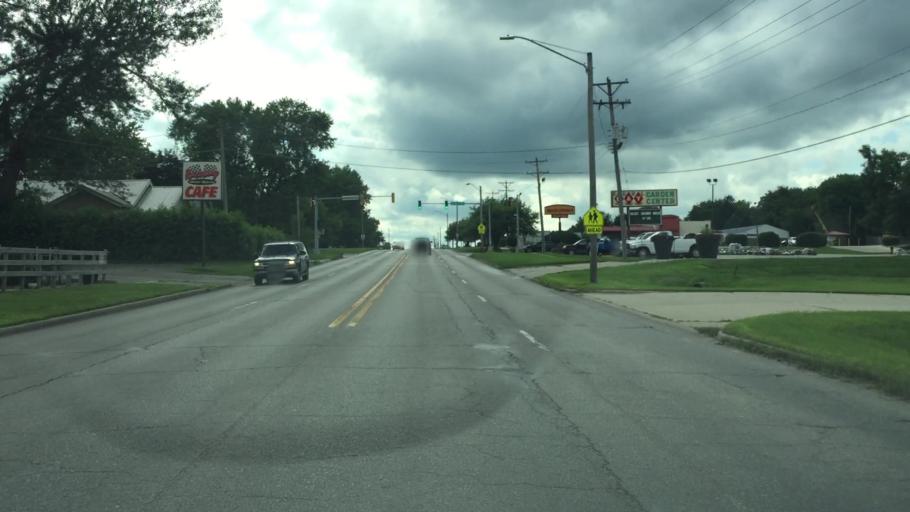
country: US
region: Iowa
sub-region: Jasper County
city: Newton
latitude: 41.6992
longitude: -93.0229
